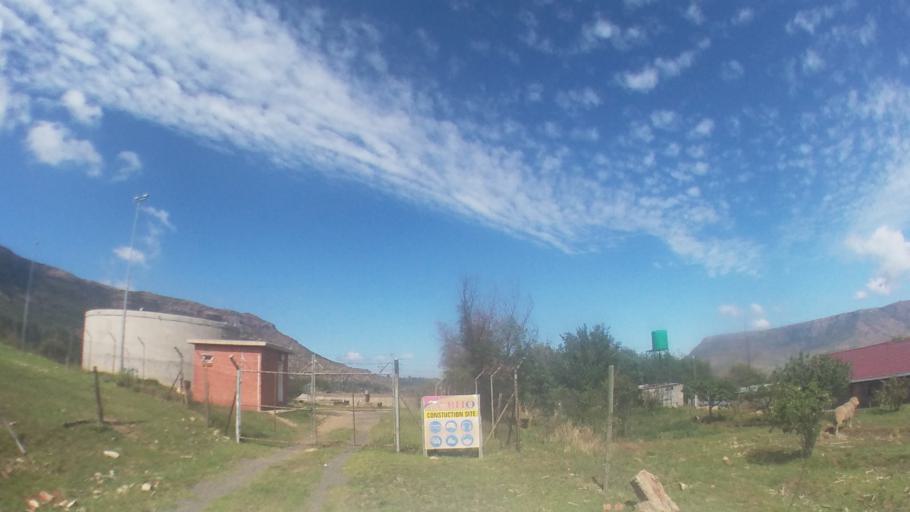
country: LS
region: Maseru
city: Nako
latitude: -29.6258
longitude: 27.5143
